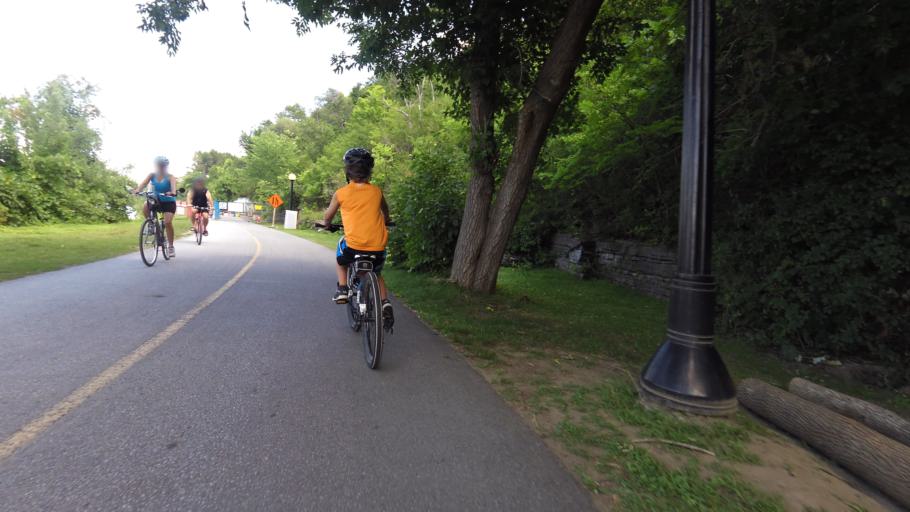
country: CA
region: Ontario
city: Ottawa
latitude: 45.4240
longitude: -75.7024
